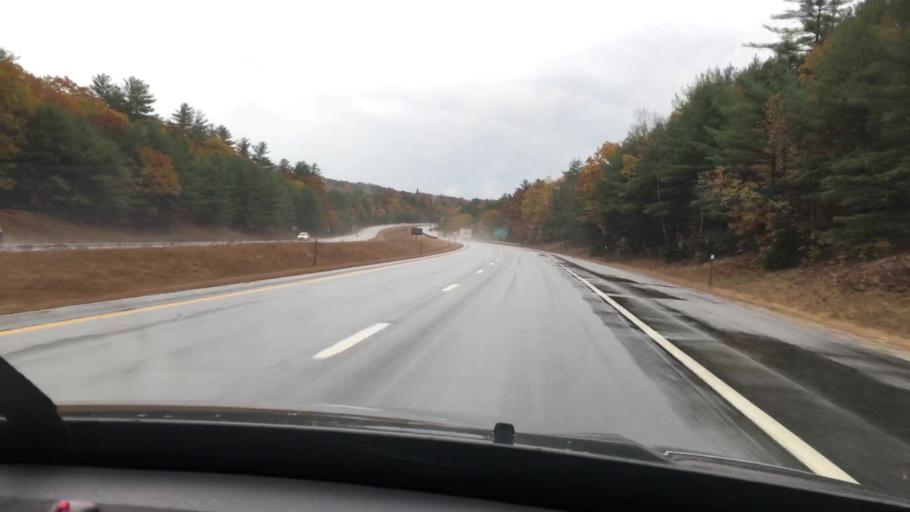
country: US
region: New Hampshire
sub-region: Grafton County
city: Ashland
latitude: 43.6259
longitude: -71.6506
